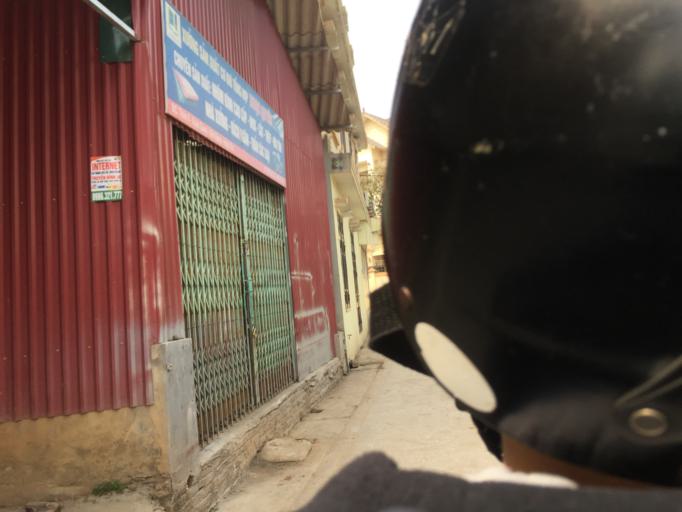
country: VN
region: Hung Yen
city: Van Giang
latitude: 20.9624
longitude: 105.9145
